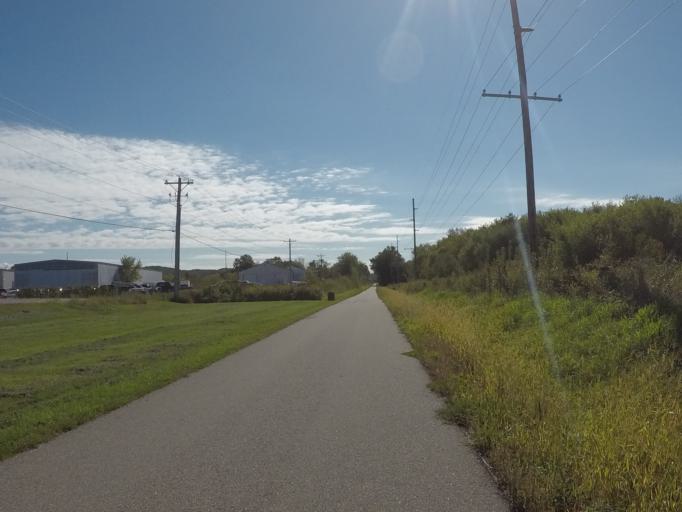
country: US
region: Wisconsin
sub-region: Richland County
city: Richland Center
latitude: 43.3164
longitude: -90.3609
